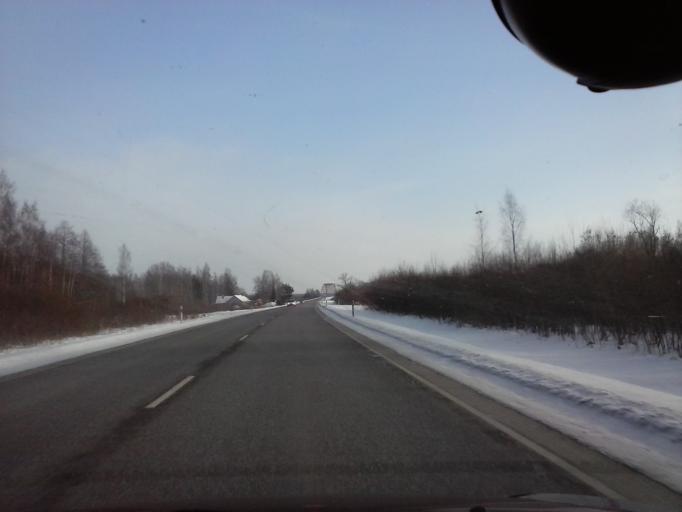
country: EE
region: Tartu
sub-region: Puhja vald
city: Puhja
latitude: 58.3913
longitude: 26.1260
